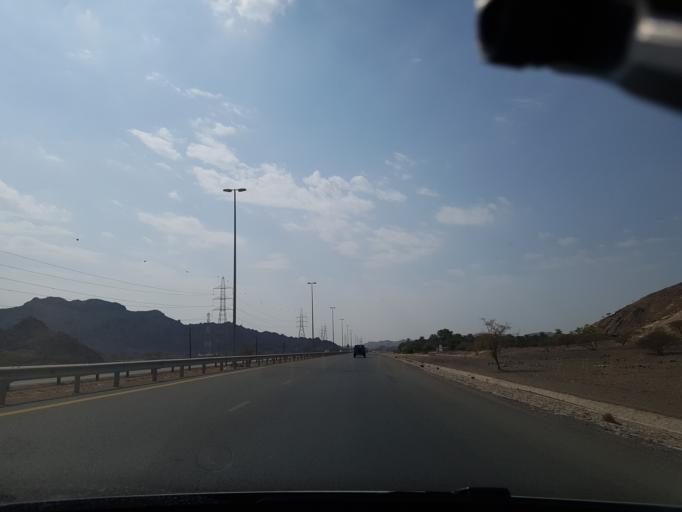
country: AE
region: Al Fujayrah
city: Dibba Al-Fujairah
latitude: 25.4918
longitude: 56.0522
